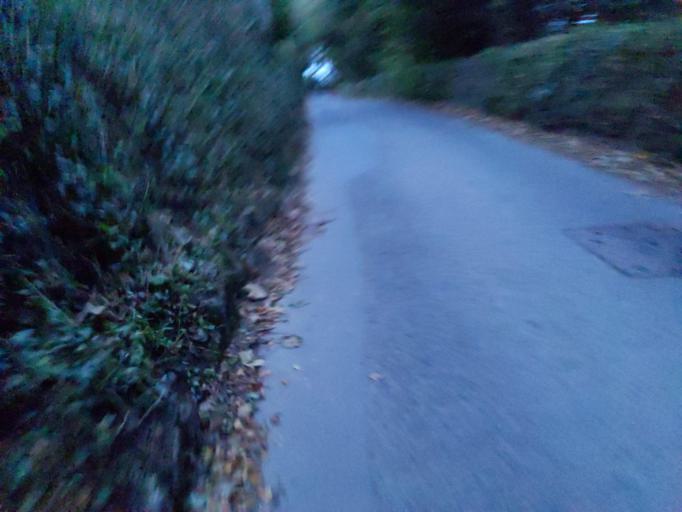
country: GB
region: England
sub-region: Devon
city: Salcombe
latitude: 50.2274
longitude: -3.7833
